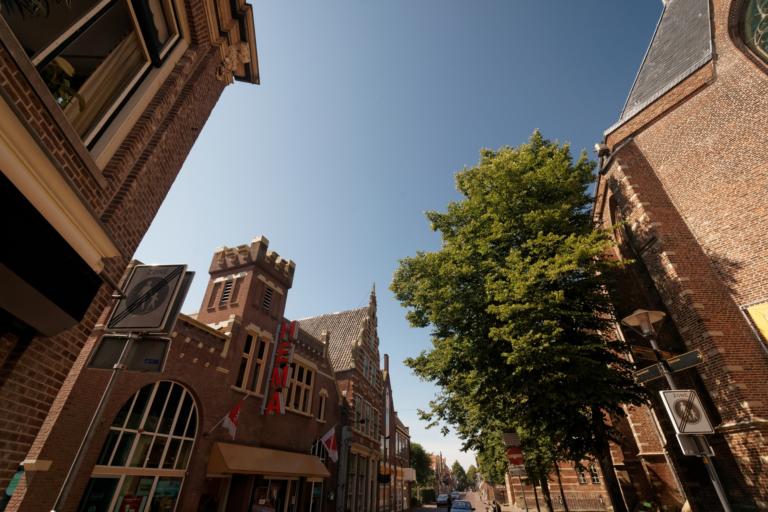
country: NL
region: North Holland
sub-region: Gemeente Enkhuizen
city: Enkhuizen
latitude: 52.7033
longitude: 5.2873
